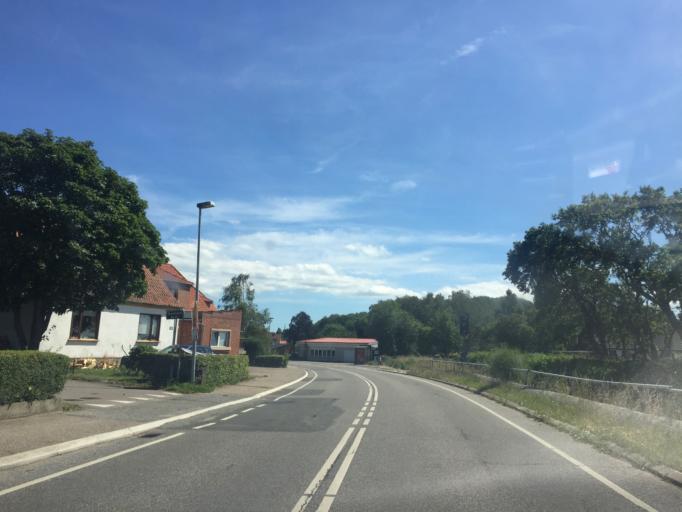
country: DK
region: Capital Region
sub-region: Halsnaes Kommune
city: Frederiksvaerk
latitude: 55.9561
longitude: 12.0215
